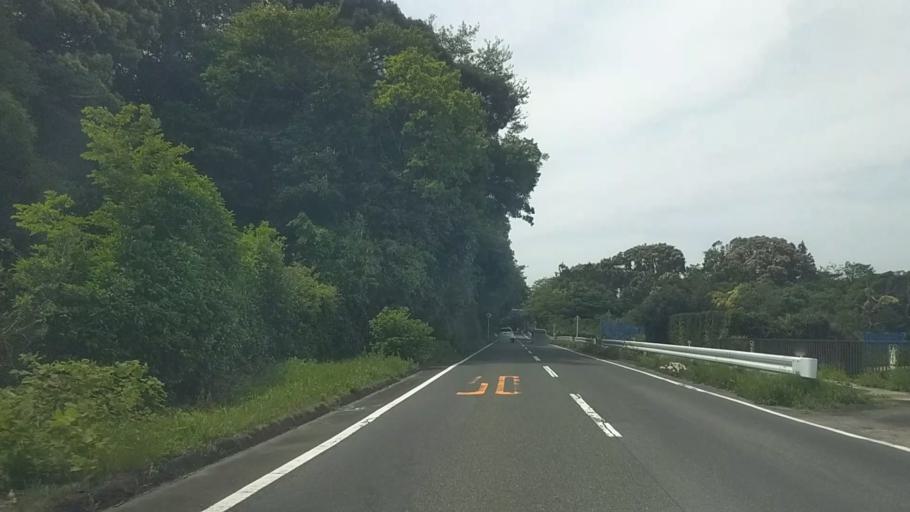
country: JP
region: Shizuoka
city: Kosai-shi
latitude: 34.7711
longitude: 137.5564
